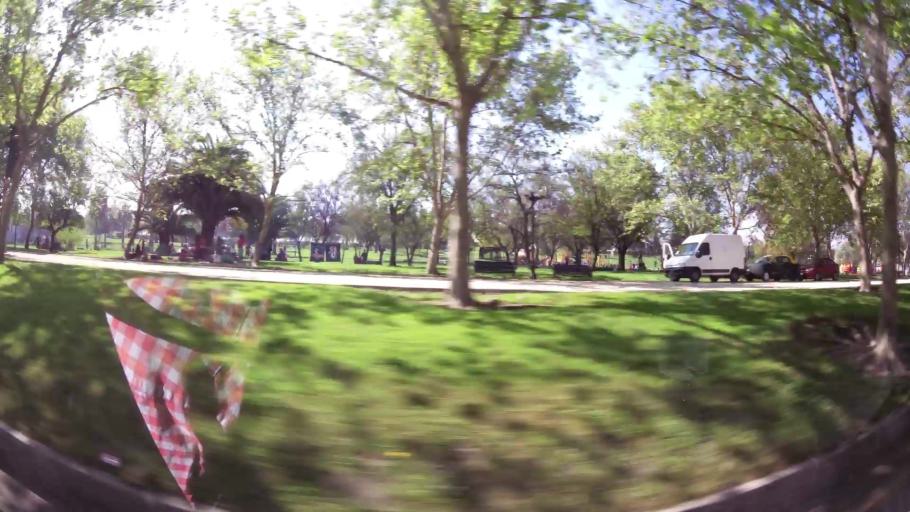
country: CL
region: Santiago Metropolitan
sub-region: Provincia de Santiago
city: Santiago
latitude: -33.4274
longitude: -70.6745
